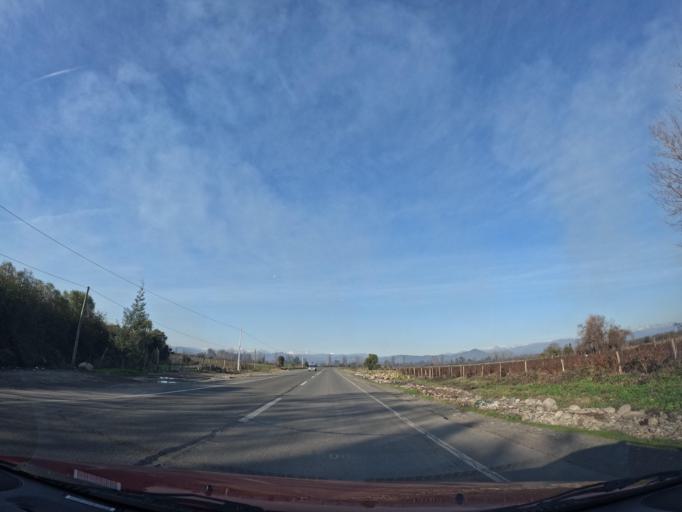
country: CL
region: Maule
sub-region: Provincia de Linares
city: Colbun
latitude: -35.6281
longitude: -71.4523
